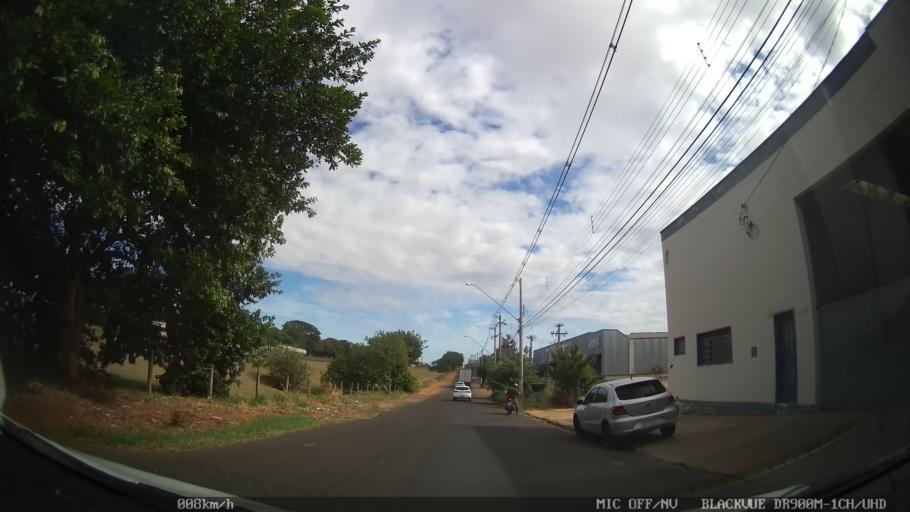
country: BR
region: Sao Paulo
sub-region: Sao Jose Do Rio Preto
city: Sao Jose do Rio Preto
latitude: -20.8089
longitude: -49.4994
